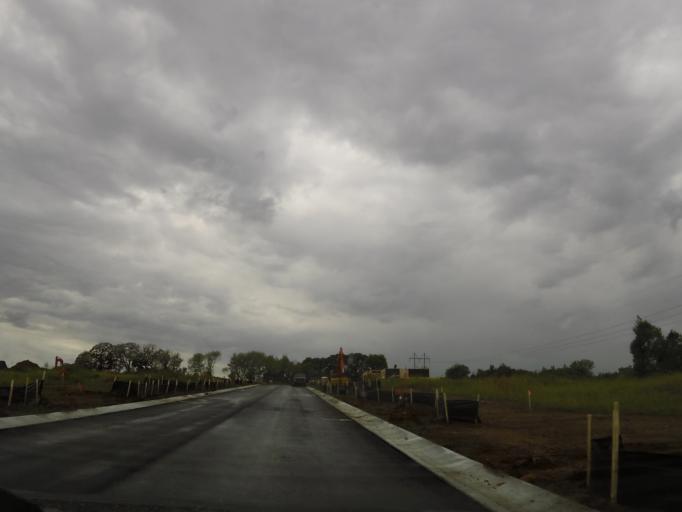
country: US
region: Minnesota
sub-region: Washington County
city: Lake Elmo
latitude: 44.9557
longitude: -92.9110
